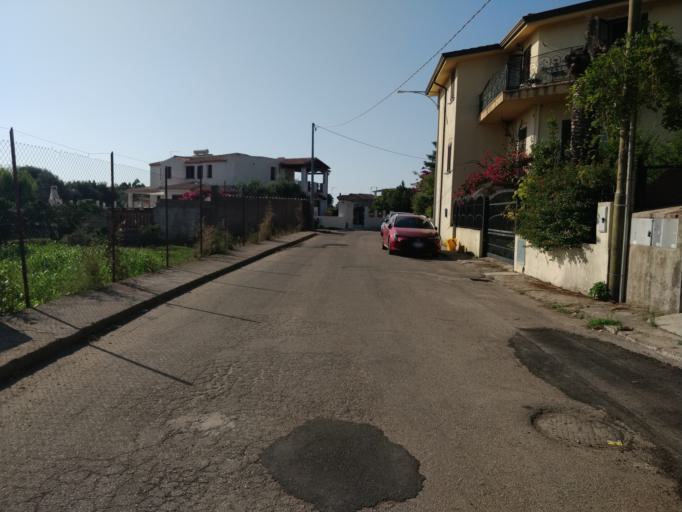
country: IT
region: Sardinia
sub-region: Provincia di Ogliastra
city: Girasole
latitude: 39.9539
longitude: 9.6634
